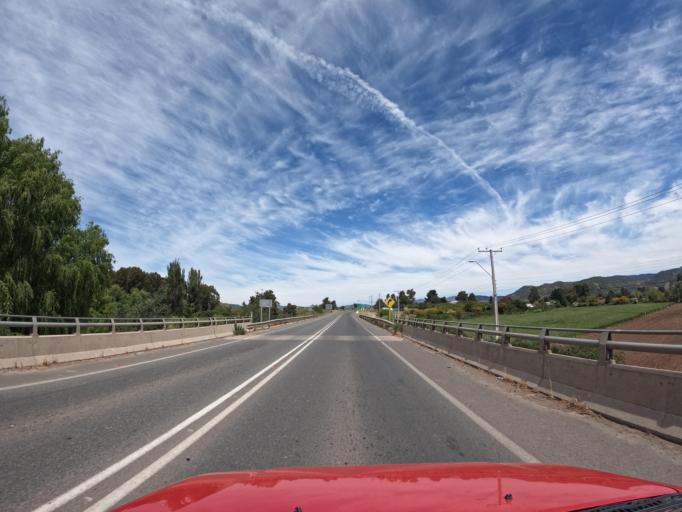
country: CL
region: Maule
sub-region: Provincia de Talca
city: Talca
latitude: -35.1079
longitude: -71.6294
